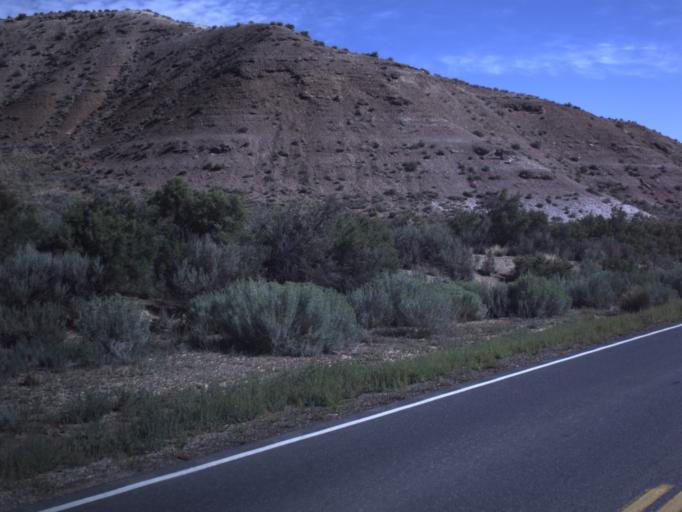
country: US
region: Utah
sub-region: Duchesne County
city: Duchesne
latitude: 40.1319
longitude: -110.4309
